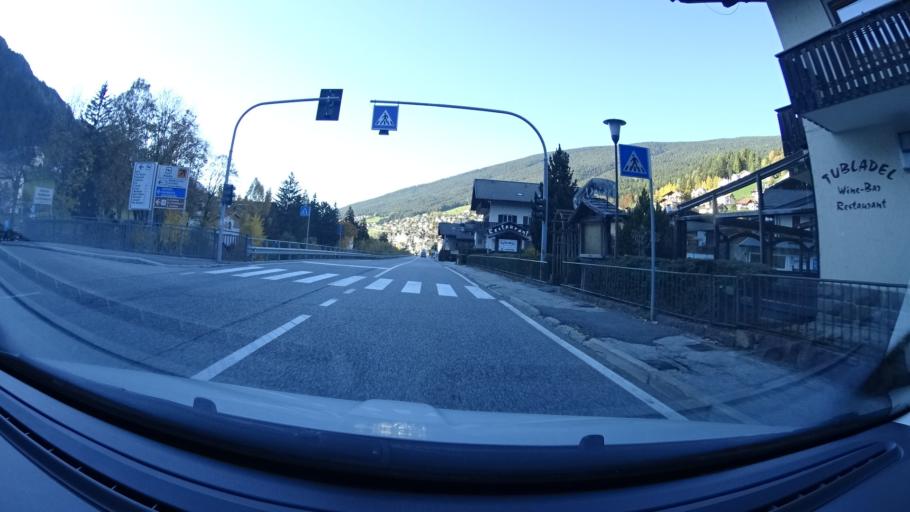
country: IT
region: Trentino-Alto Adige
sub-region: Bolzano
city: Ortisei
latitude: 46.5705
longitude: 11.6790
